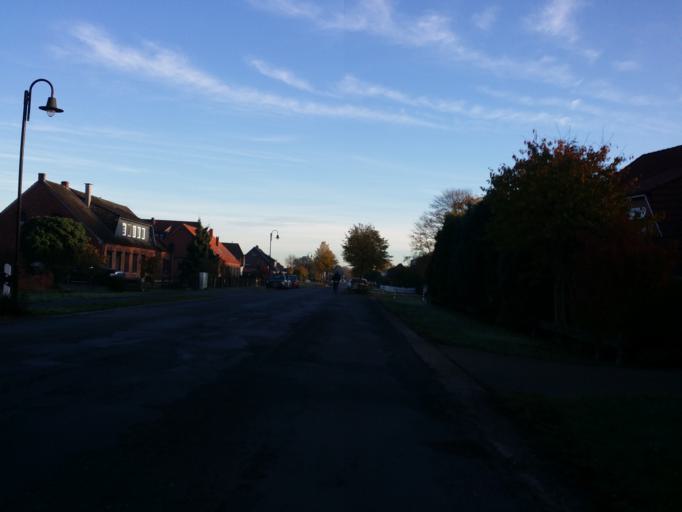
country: DE
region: Lower Saxony
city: Stuhr
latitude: 52.9979
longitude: 8.7700
